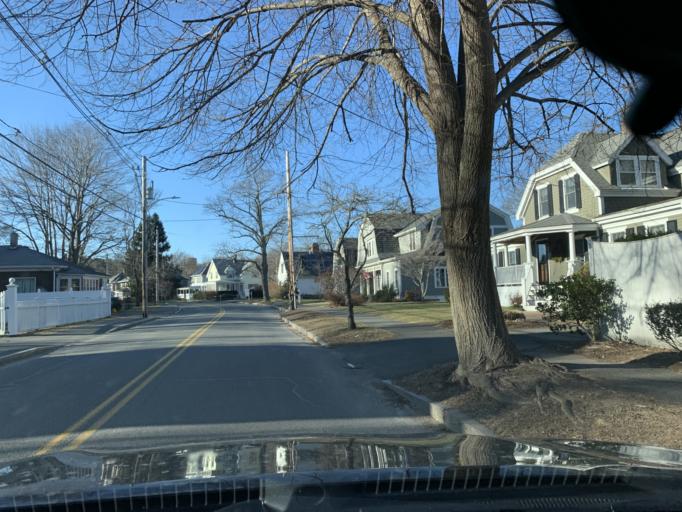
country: US
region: Massachusetts
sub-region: Essex County
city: Essex
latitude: 42.5834
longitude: -70.7708
